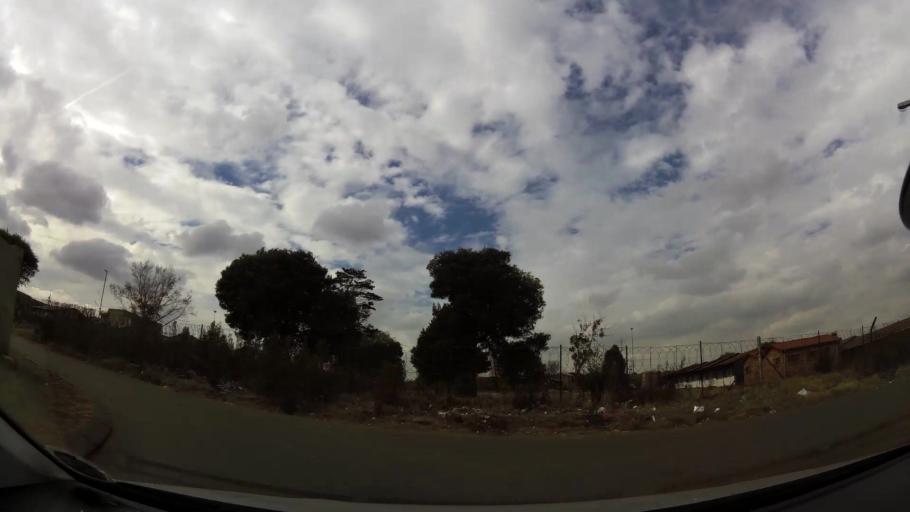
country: ZA
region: Gauteng
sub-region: City of Johannesburg Metropolitan Municipality
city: Soweto
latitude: -26.2756
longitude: 27.8492
